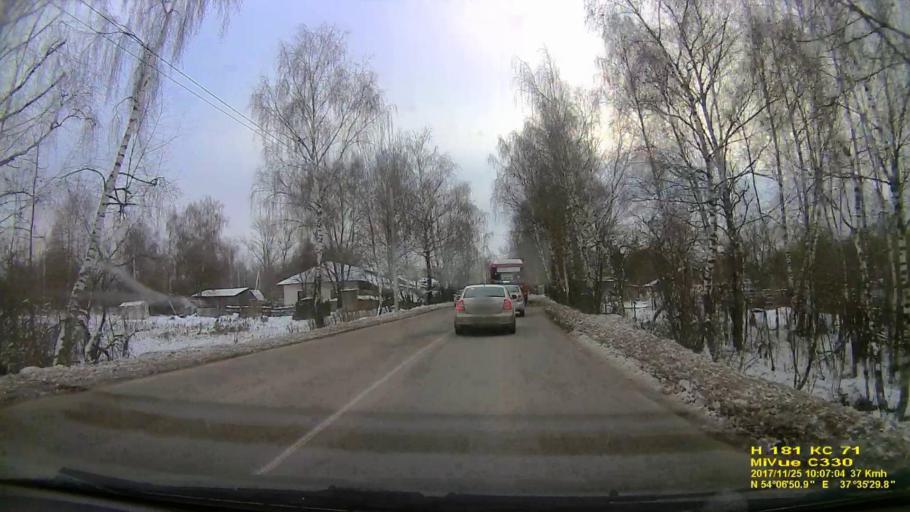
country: RU
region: Tula
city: Skuratovskiy
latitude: 54.1141
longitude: 37.5917
